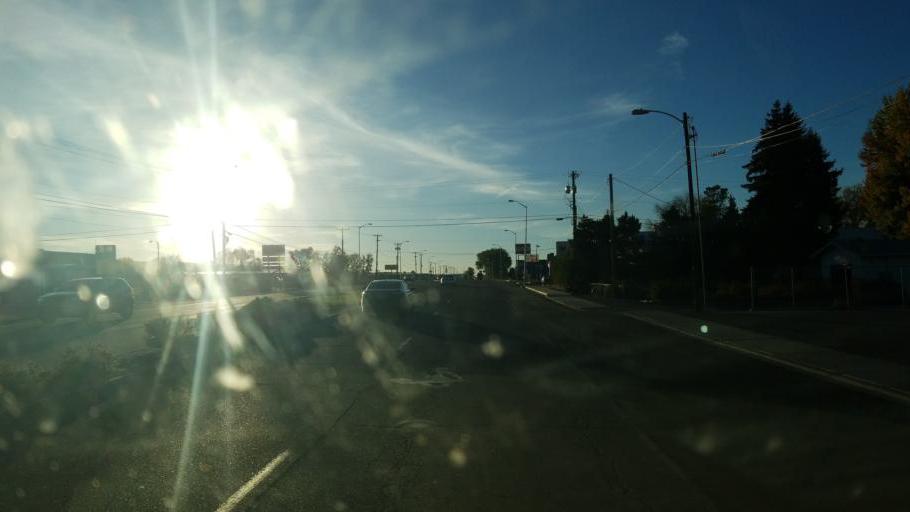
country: US
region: New Mexico
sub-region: San Juan County
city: Farmington
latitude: 36.7194
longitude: -108.1726
